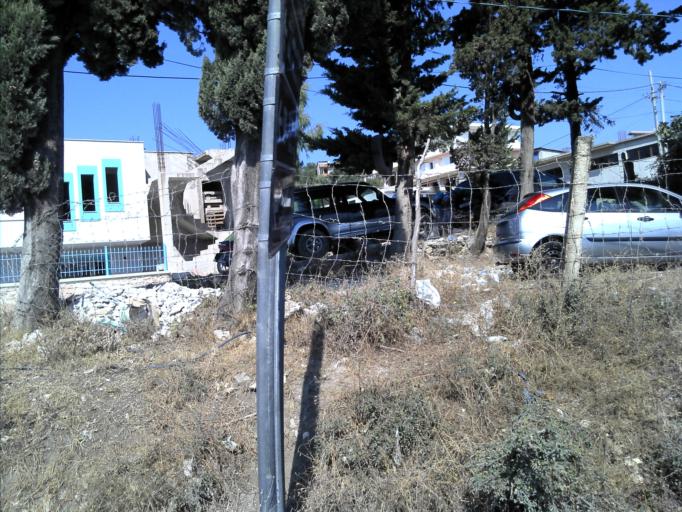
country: AL
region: Vlore
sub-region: Rrethi i Sarandes
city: Sarande
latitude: 39.8756
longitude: 20.0303
